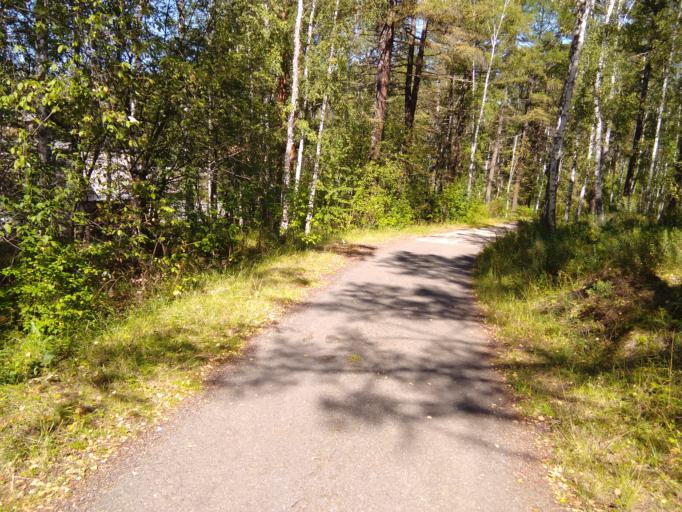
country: RU
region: Bashkortostan
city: Abzakovo
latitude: 53.8138
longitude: 58.6033
